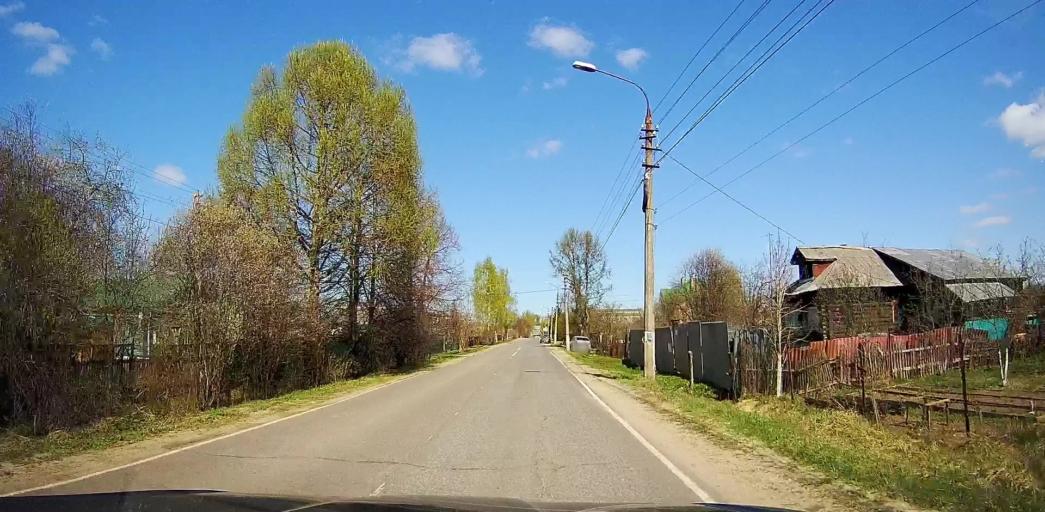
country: RU
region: Moskovskaya
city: Ramenskoye
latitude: 55.6213
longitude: 38.3024
